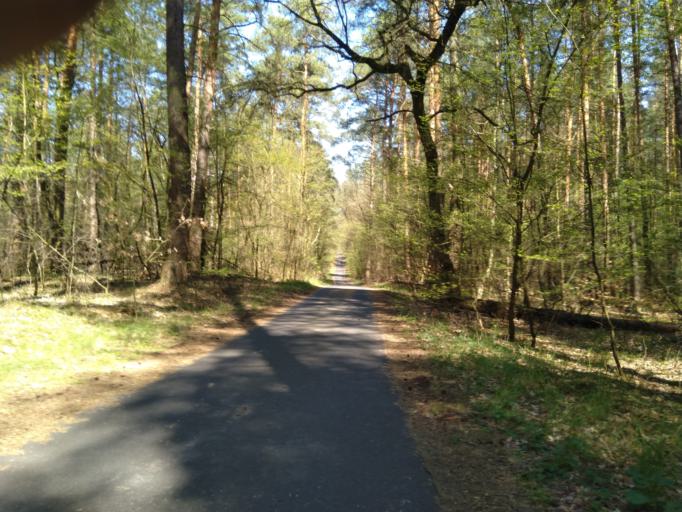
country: DE
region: Brandenburg
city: Rudnitz
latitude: 52.7318
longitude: 13.6044
